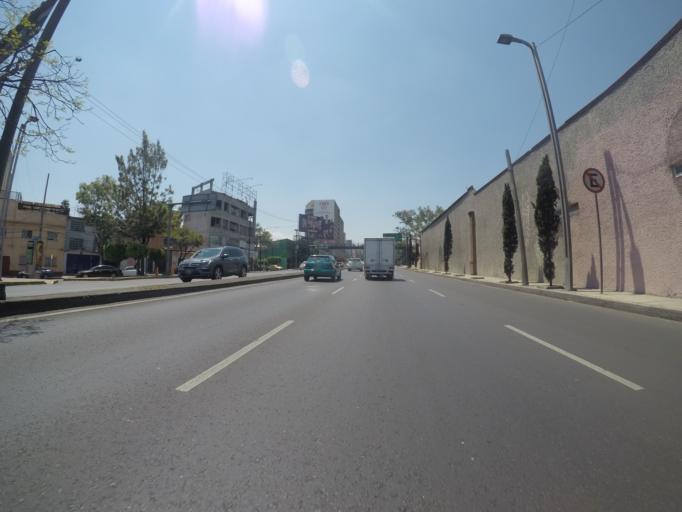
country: MX
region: Mexico City
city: Polanco
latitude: 19.4095
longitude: -99.1967
